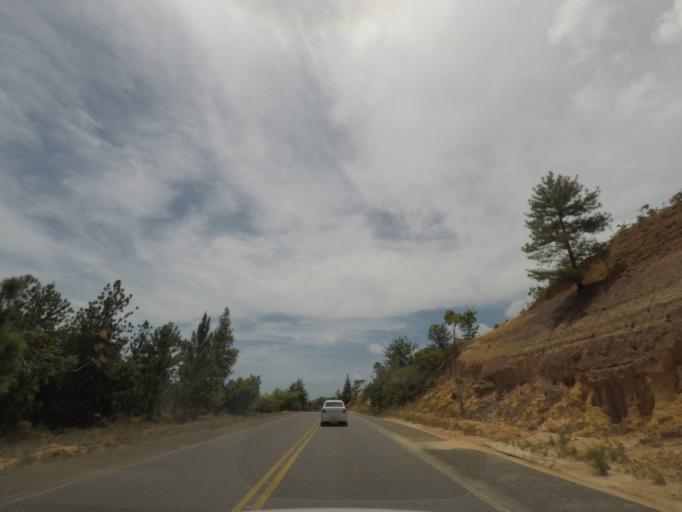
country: BR
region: Bahia
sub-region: Conde
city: Conde
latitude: -12.0021
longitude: -37.6837
